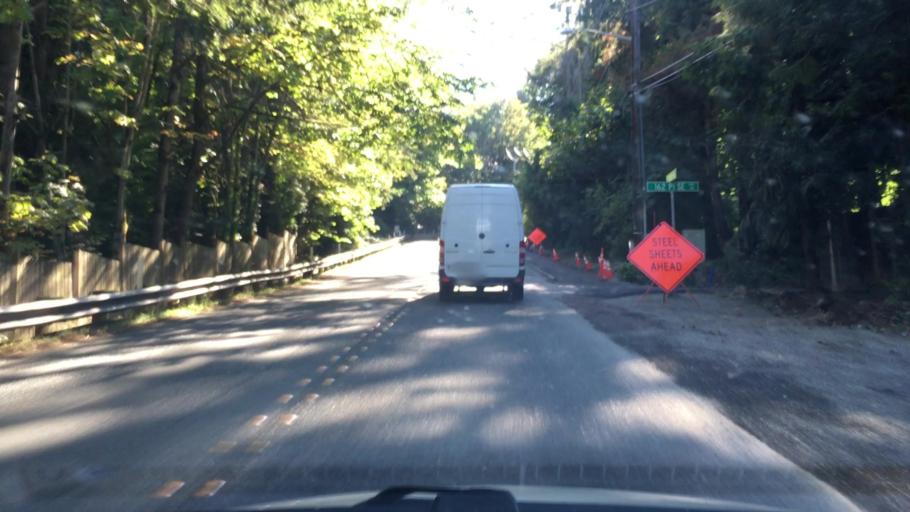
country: US
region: Washington
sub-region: King County
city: West Lake Sammamish
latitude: 47.5788
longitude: -122.1236
